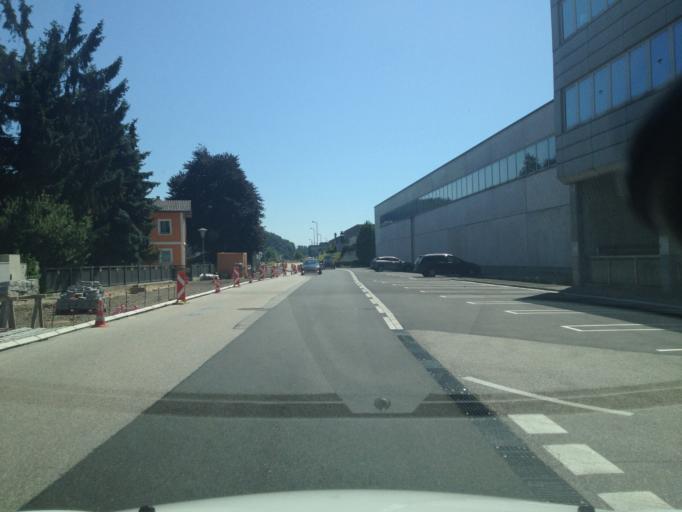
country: AT
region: Upper Austria
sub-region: Politischer Bezirk Urfahr-Umgebung
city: Steyregg
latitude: 48.2835
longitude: 14.3618
